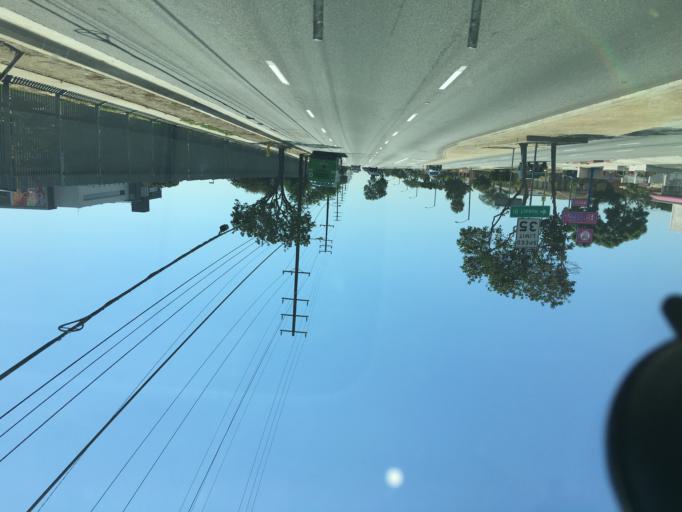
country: US
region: California
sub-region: Los Angeles County
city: West Athens
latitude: 33.9309
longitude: -118.3083
